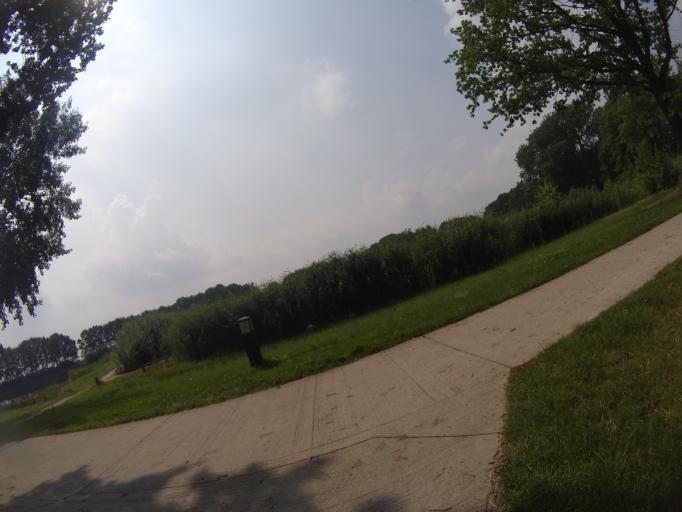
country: NL
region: Drenthe
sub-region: Gemeente Emmen
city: Emmer-Compascuum
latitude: 52.8055
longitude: 7.0314
